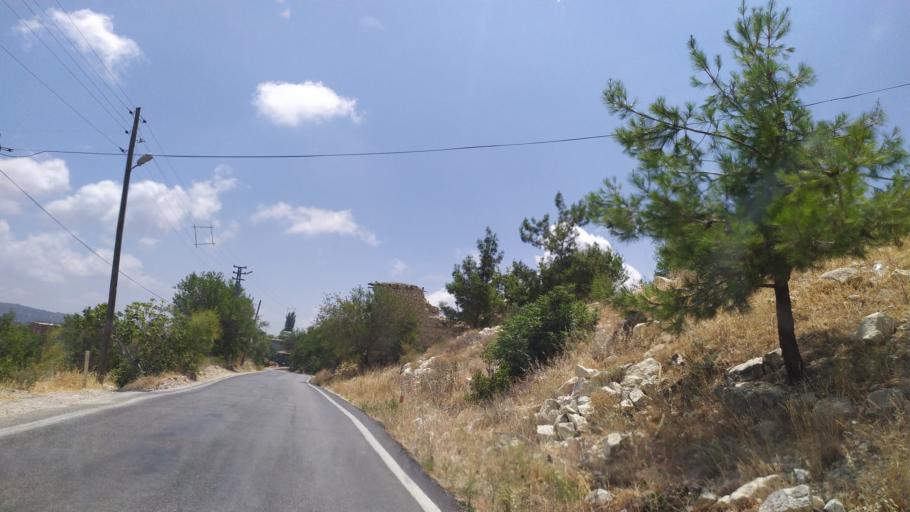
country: TR
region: Mersin
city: Gulnar
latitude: 36.2864
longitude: 33.3832
